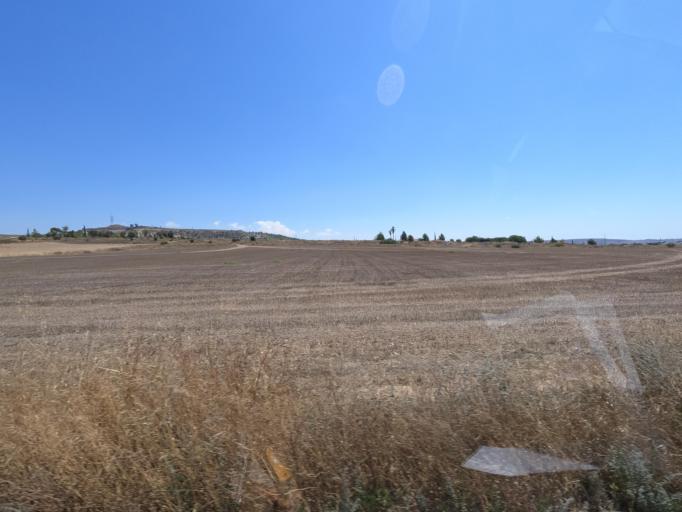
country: CY
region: Larnaka
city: Voroklini
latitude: 34.9975
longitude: 33.6664
